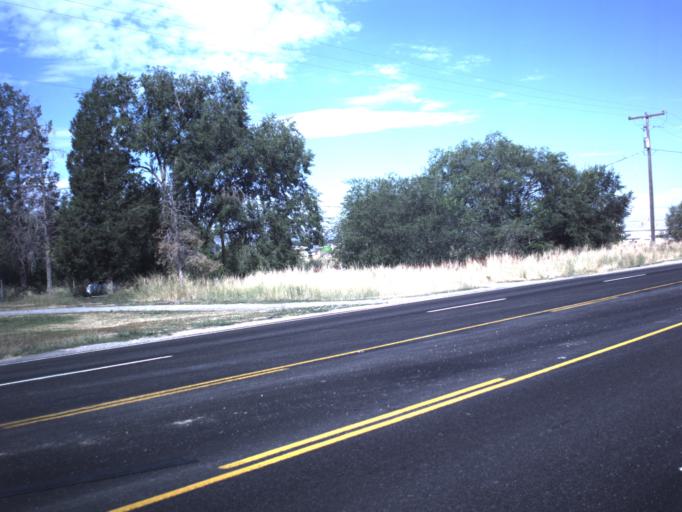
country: US
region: Utah
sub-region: Weber County
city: Pleasant View
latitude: 41.3131
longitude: -112.0105
